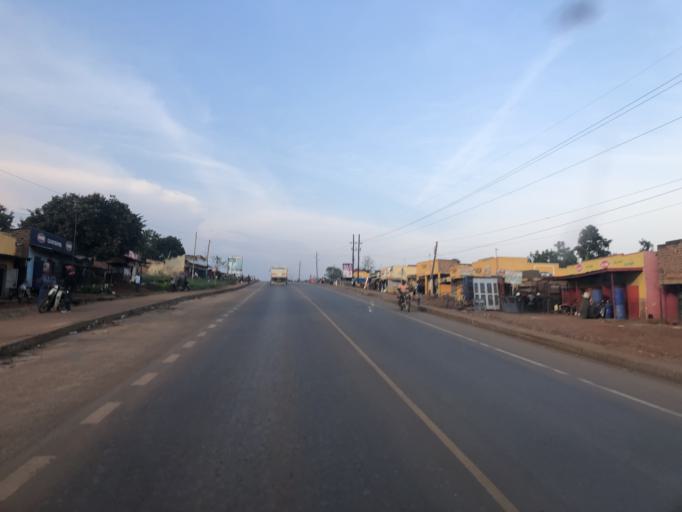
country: UG
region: Central Region
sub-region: Mpigi District
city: Mpigi
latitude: 0.2063
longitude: 32.3136
